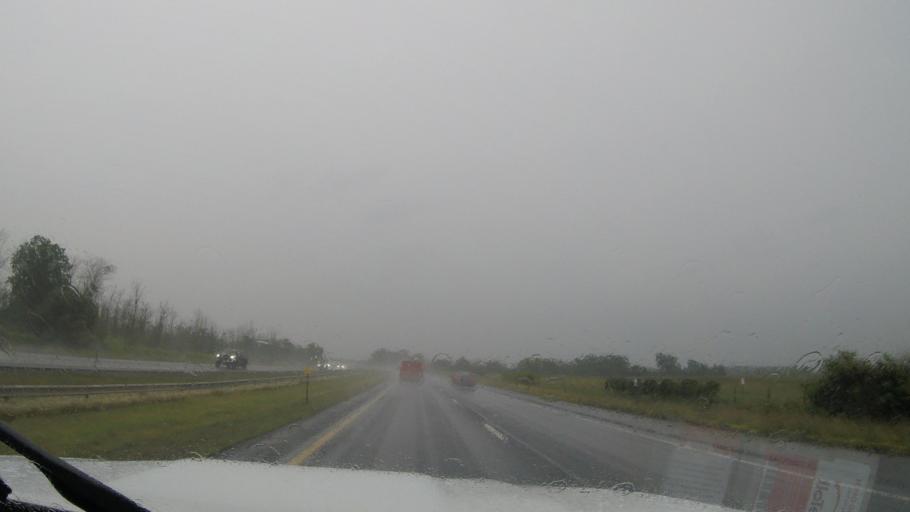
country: US
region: New York
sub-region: Seneca County
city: Bridgeport
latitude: 42.9843
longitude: -76.7774
